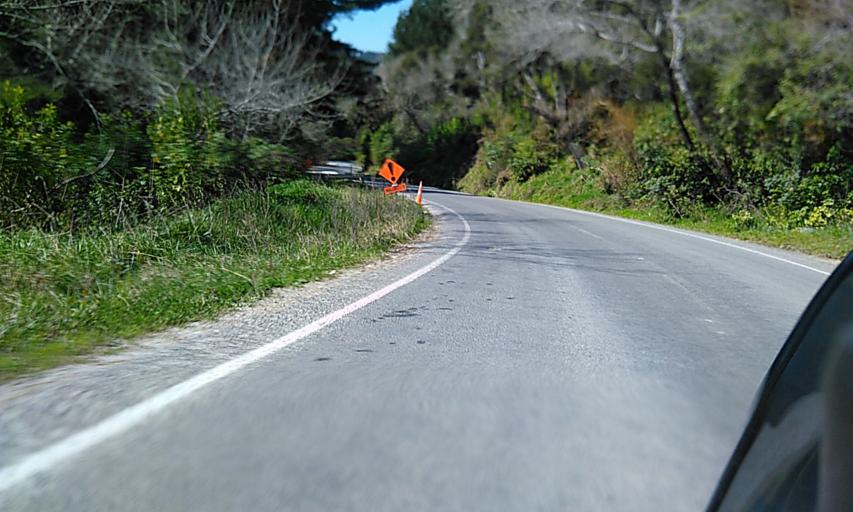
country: NZ
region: Gisborne
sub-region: Gisborne District
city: Gisborne
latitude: -38.3184
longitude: 178.1372
